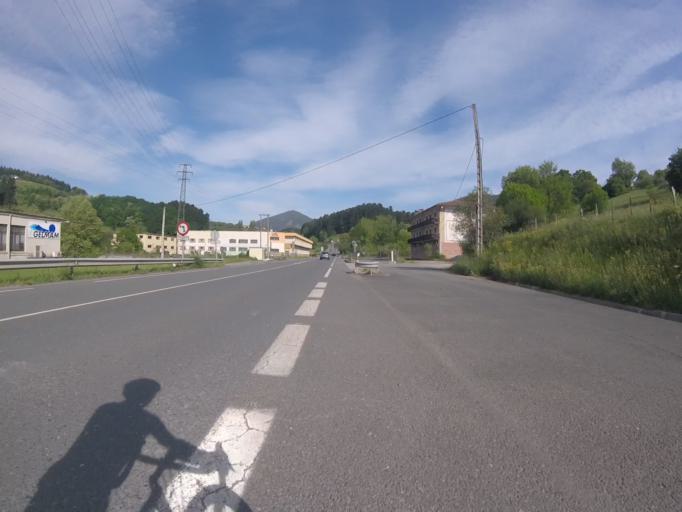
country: ES
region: Basque Country
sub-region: Provincia de Guipuzcoa
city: Zumarraga
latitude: 43.0791
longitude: -2.2951
